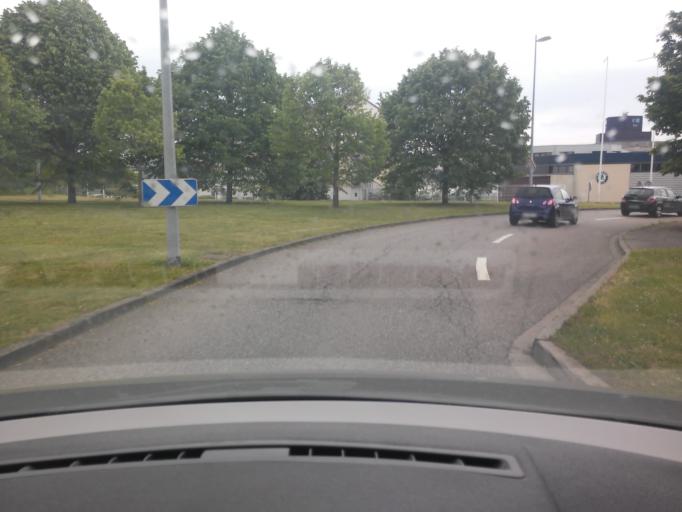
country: FR
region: Lorraine
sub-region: Departement de Meurthe-et-Moselle
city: Laxou
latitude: 48.6908
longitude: 6.1339
